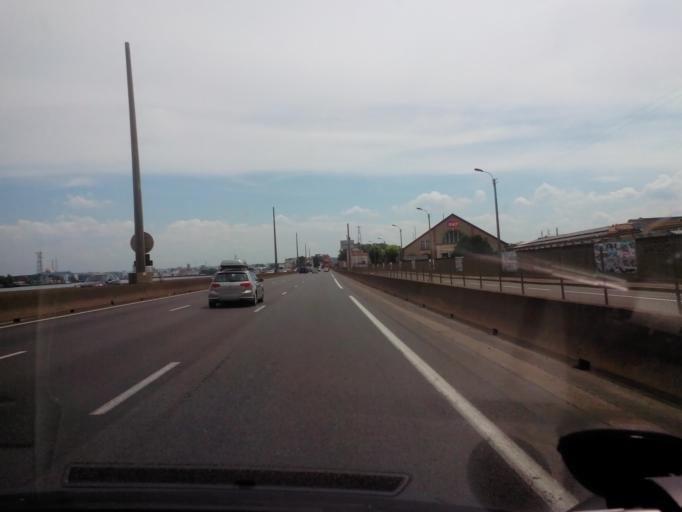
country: FR
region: Rhone-Alpes
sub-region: Departement du Rhone
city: La Mulatiere
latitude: 45.7236
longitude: 4.8174
